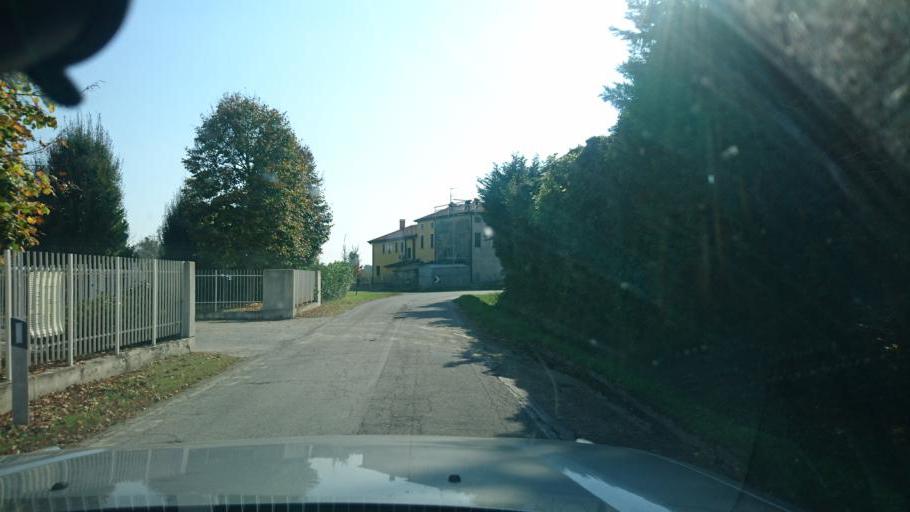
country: IT
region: Veneto
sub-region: Provincia di Padova
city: Rubano
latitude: 45.4102
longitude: 11.7970
